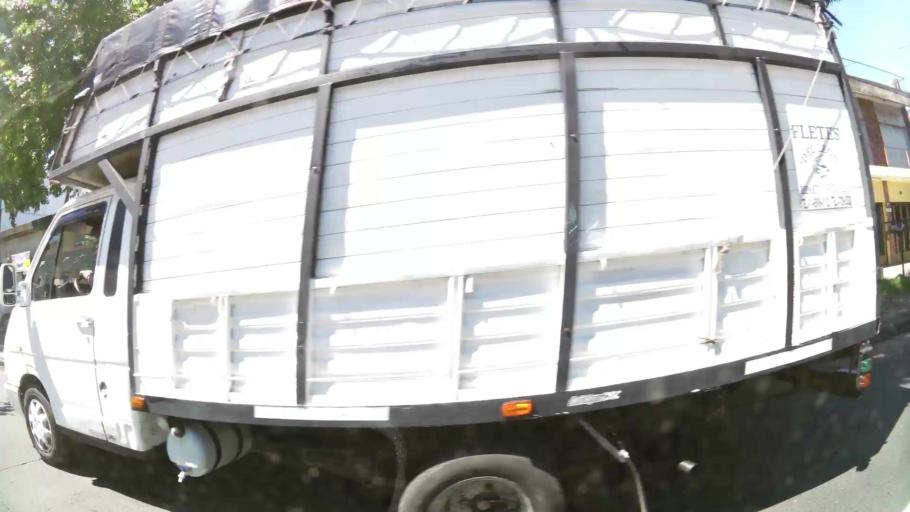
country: AR
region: Buenos Aires
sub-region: Partido de General San Martin
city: General San Martin
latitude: -34.5111
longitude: -58.5760
